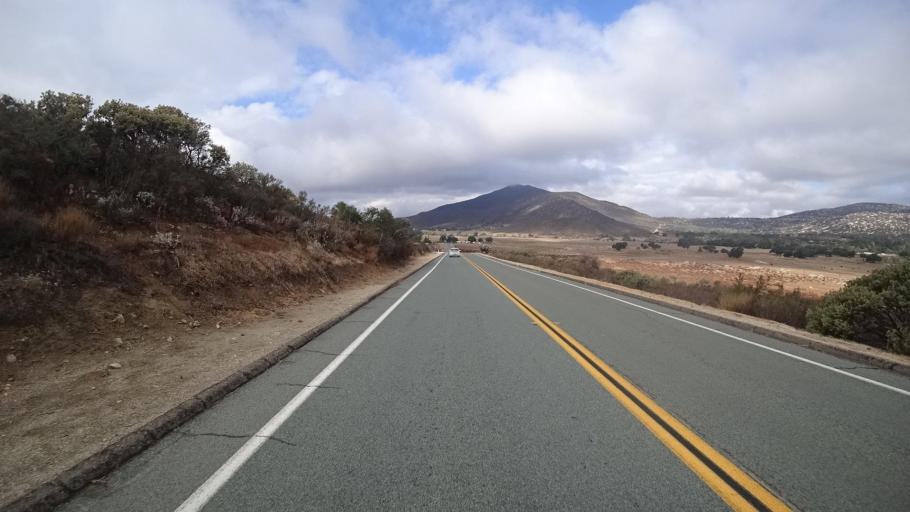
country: MX
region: Baja California
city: Tecate
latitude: 32.6152
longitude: -116.6066
